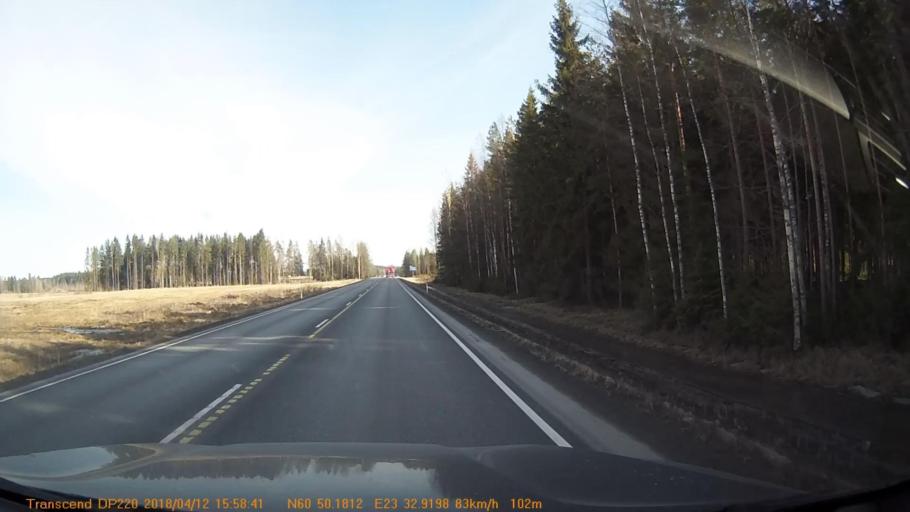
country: FI
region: Haeme
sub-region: Forssa
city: Forssa
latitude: 60.8358
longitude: 23.5500
